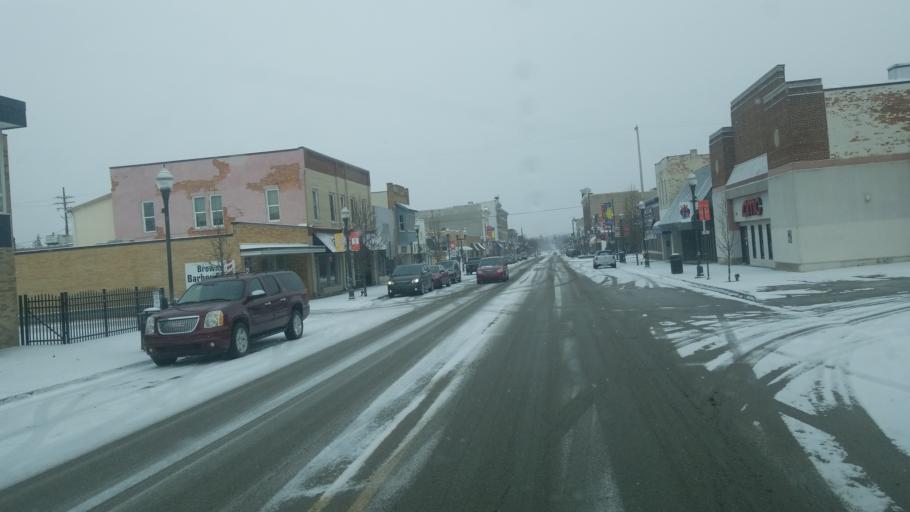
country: US
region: Michigan
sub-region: Mecosta County
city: Big Rapids
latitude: 43.6961
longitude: -85.4819
